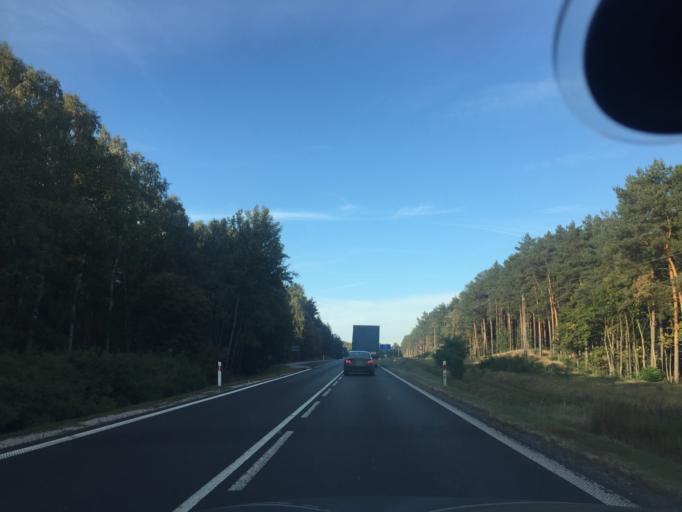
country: PL
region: Kujawsko-Pomorskie
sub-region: Powiat torunski
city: Wielka Nieszawka
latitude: 52.9201
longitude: 18.4982
